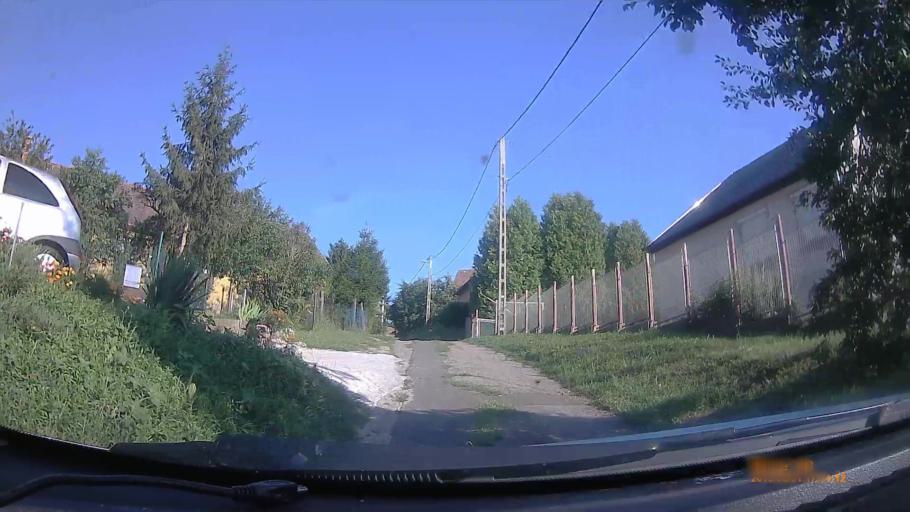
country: HU
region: Baranya
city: Sasd
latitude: 46.1910
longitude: 18.1484
